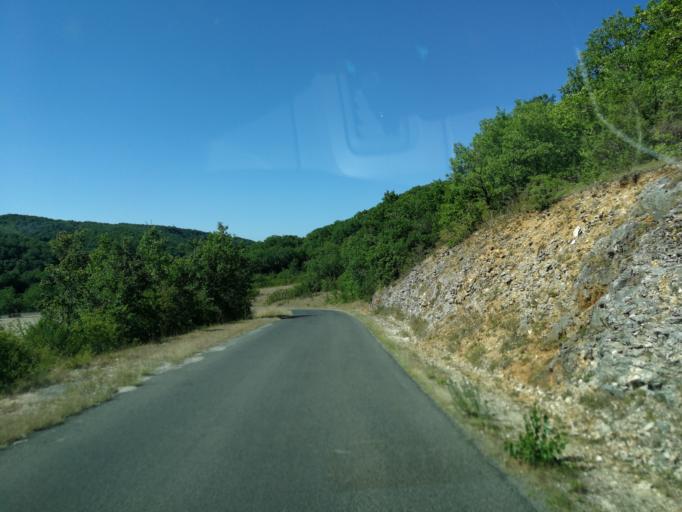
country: FR
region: Midi-Pyrenees
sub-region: Departement du Lot
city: Souillac
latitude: 44.9072
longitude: 1.4793
